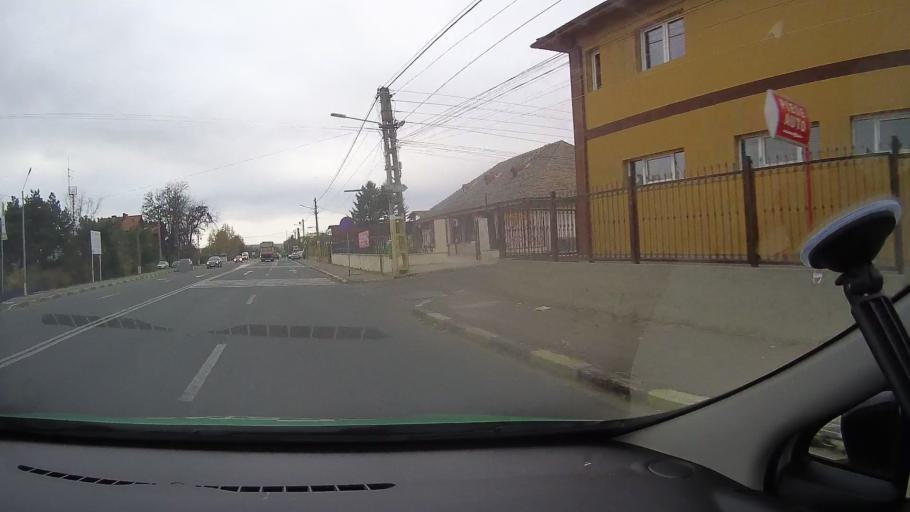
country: RO
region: Constanta
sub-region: Oras Murfatlar
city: Murfatlar
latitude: 44.1720
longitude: 28.4193
